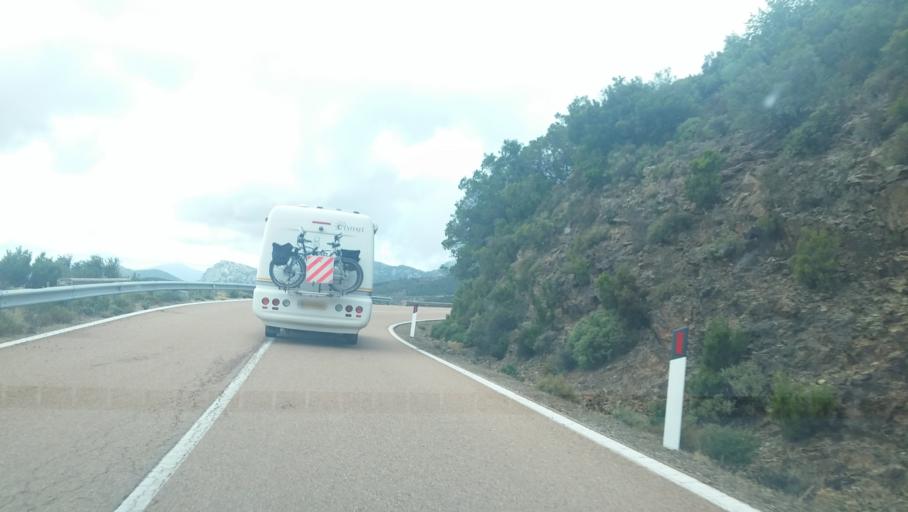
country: IT
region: Sardinia
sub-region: Provincia di Ogliastra
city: Urzulei
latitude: 40.1629
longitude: 9.5250
